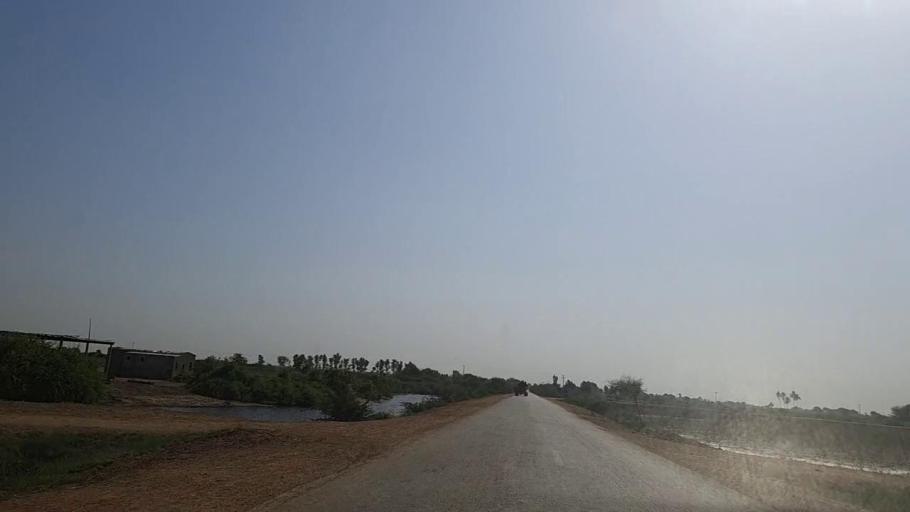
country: PK
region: Sindh
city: Mirpur Batoro
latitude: 24.6060
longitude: 68.2958
